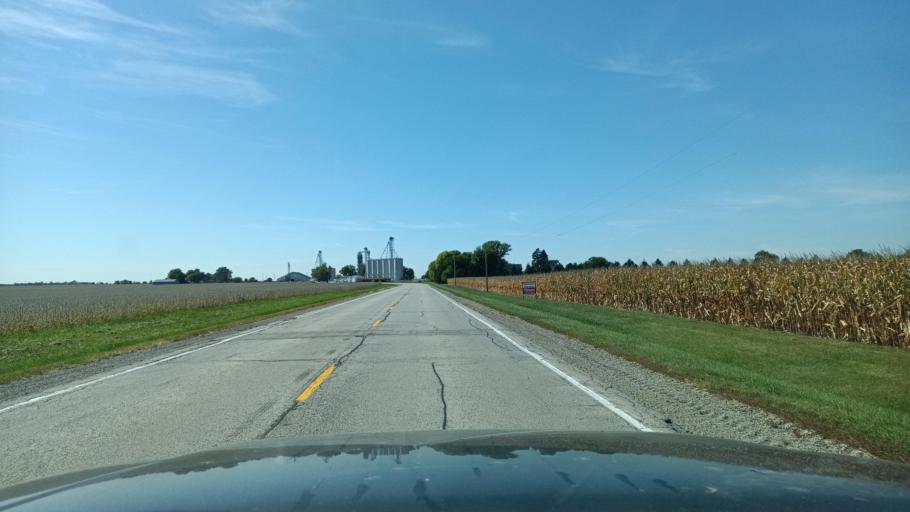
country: US
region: Illinois
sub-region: De Witt County
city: Farmer City
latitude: 40.2238
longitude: -88.7097
